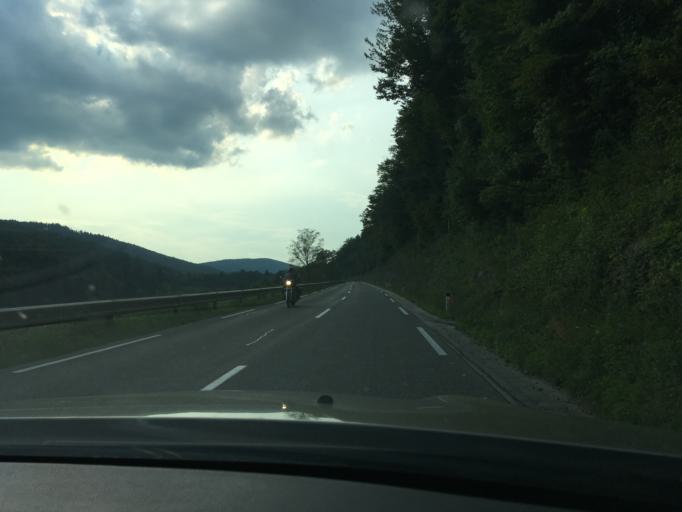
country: SI
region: Dolenjske Toplice
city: Dolenjske Toplice
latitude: 45.7854
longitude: 14.9972
